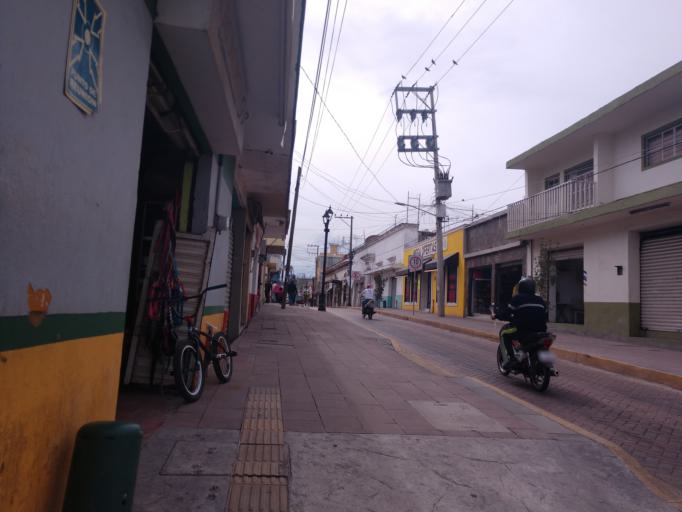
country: MX
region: Nayarit
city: Tepic
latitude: 21.5146
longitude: -104.8929
